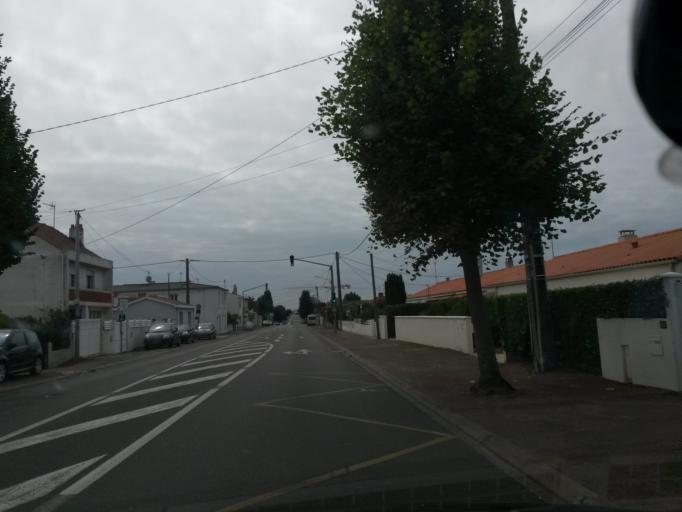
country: FR
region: Pays de la Loire
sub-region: Departement de la Vendee
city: Olonne-sur-Mer
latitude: 46.5197
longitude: -1.7757
